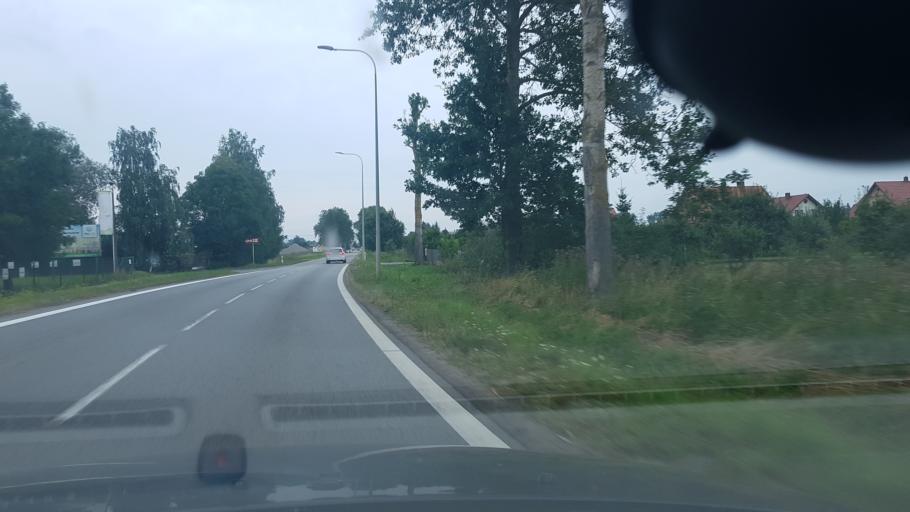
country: PL
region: Pomeranian Voivodeship
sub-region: Powiat nowodworski
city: Nowy Dwor Gdanski
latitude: 54.2159
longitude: 19.1073
